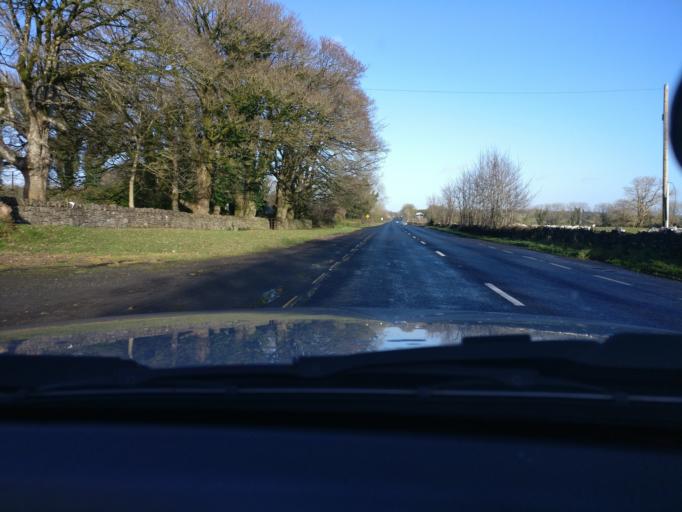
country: IE
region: Connaught
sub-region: County Galway
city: Loughrea
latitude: 53.2494
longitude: -8.4442
